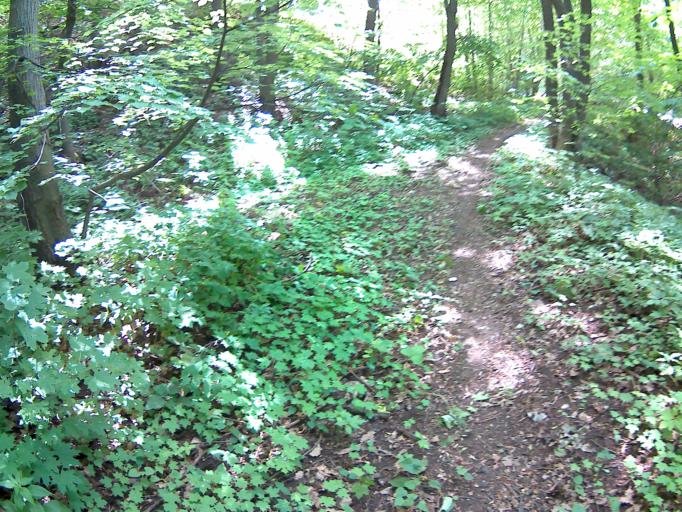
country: RU
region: Nizjnij Novgorod
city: Nizhniy Novgorod
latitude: 56.2261
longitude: 43.9208
